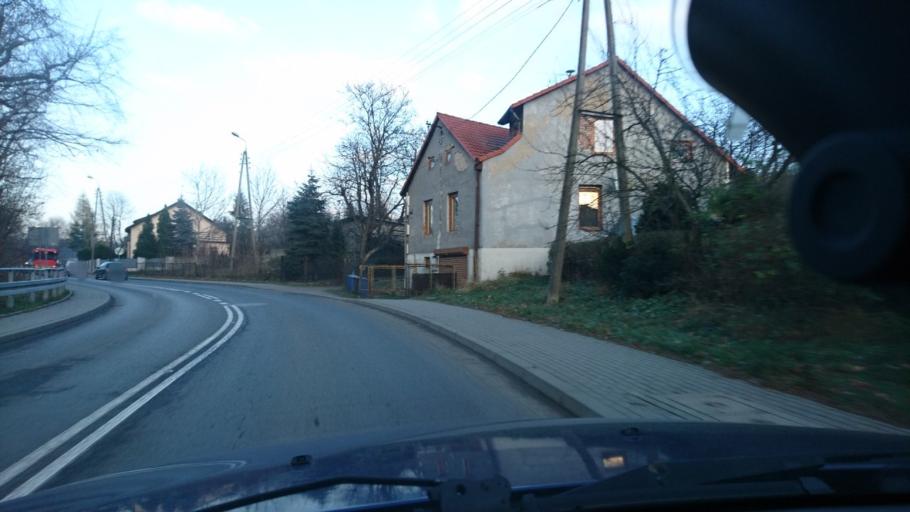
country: PL
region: Silesian Voivodeship
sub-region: Bielsko-Biala
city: Bielsko-Biala
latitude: 49.8165
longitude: 19.0798
